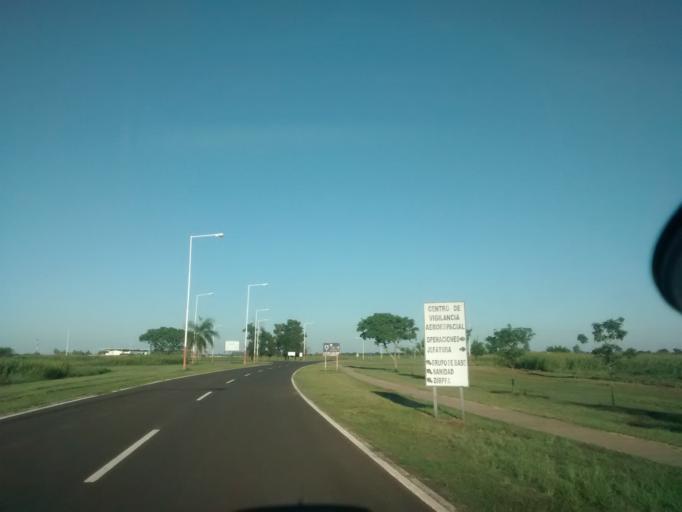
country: AR
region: Chaco
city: Fontana
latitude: -27.4429
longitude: -59.0409
